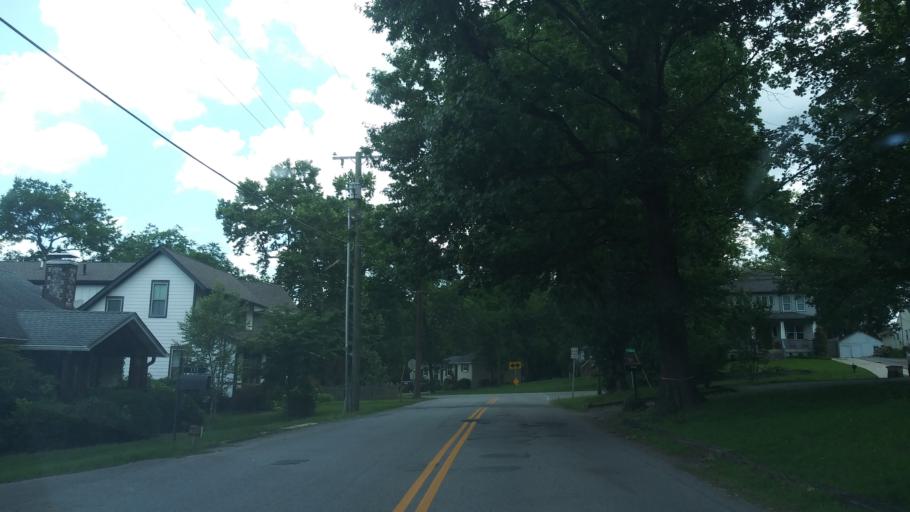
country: US
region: Tennessee
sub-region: Davidson County
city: Nashville
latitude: 36.1430
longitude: -86.8288
